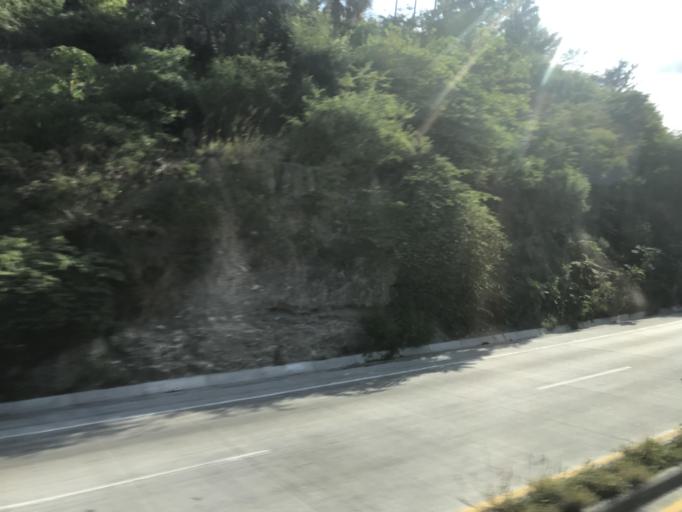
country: GT
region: El Progreso
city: Guastatoya
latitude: 14.8541
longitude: -90.1007
